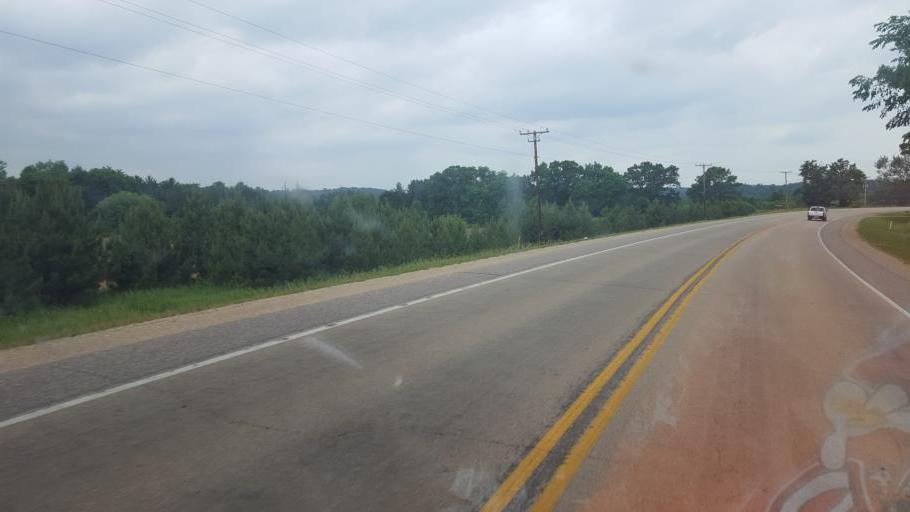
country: US
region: Wisconsin
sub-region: Juneau County
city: Elroy
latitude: 43.6359
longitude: -90.1792
